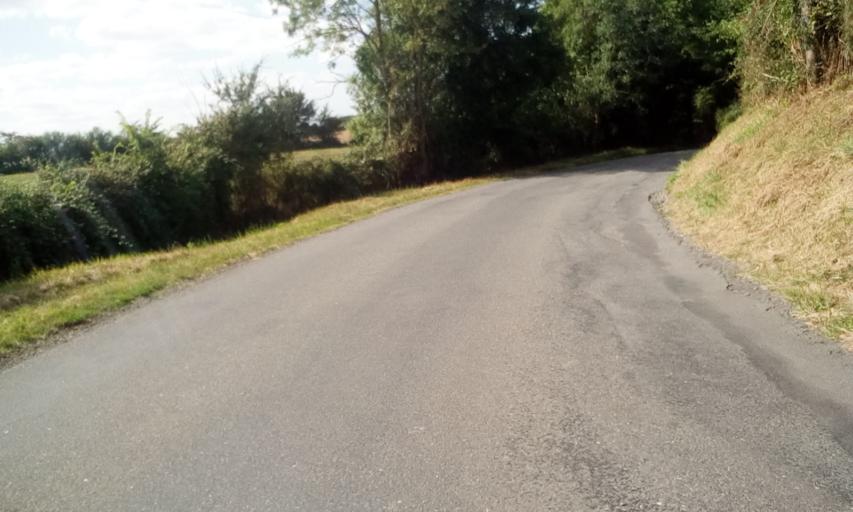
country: FR
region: Lower Normandy
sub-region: Departement du Calvados
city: Argences
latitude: 49.1544
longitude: -0.1497
